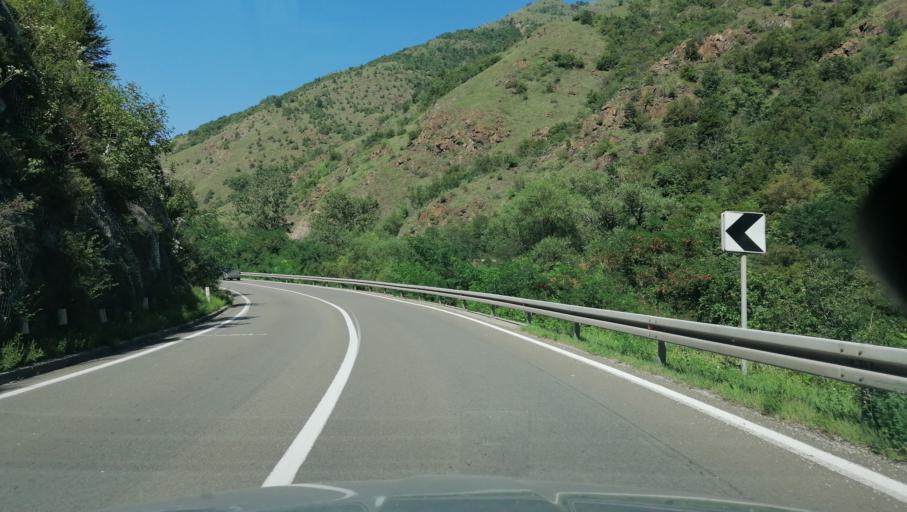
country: RS
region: Central Serbia
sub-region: Raski Okrug
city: Kraljevo
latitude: 43.6006
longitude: 20.5591
